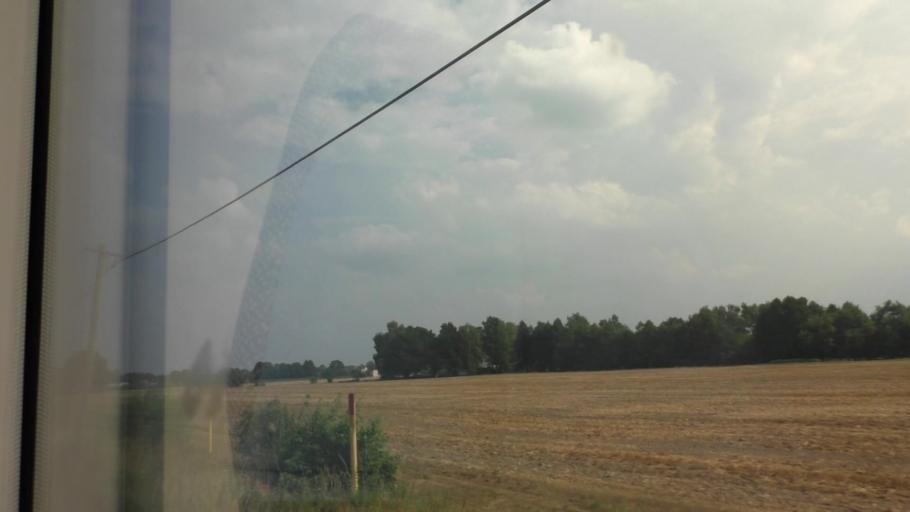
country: DE
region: Brandenburg
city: Bestensee
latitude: 52.2956
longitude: 13.7596
